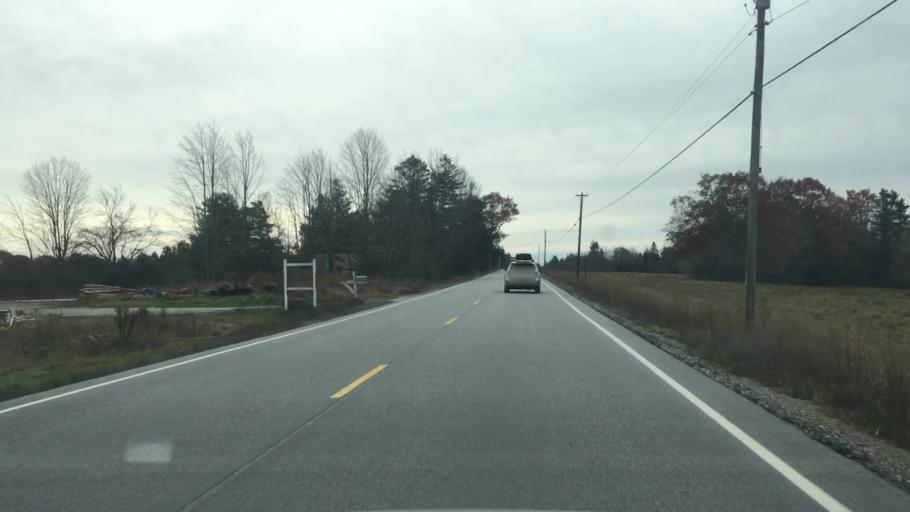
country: US
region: Maine
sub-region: Hancock County
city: Penobscot
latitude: 44.4822
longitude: -68.6399
